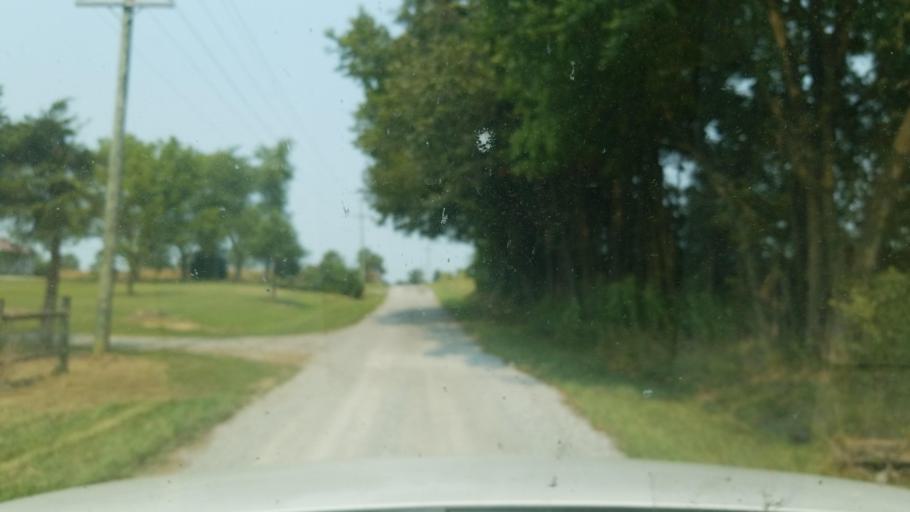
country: US
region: Illinois
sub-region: Saline County
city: Eldorado
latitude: 37.8136
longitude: -88.5167
